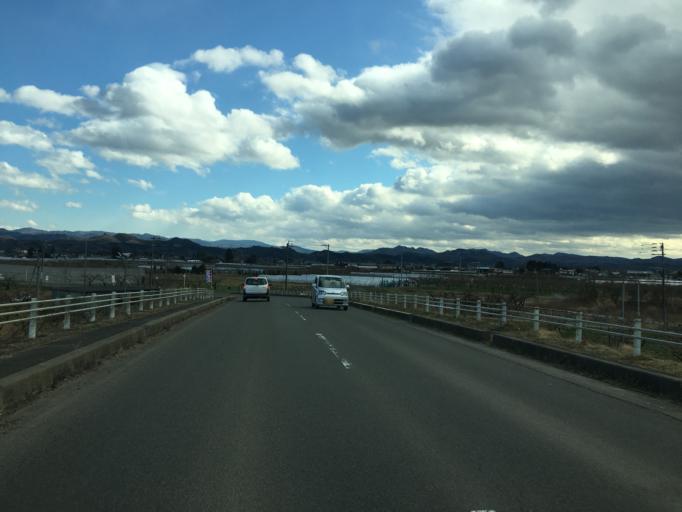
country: JP
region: Fukushima
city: Yanagawamachi-saiwaicho
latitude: 37.8607
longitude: 140.5702
